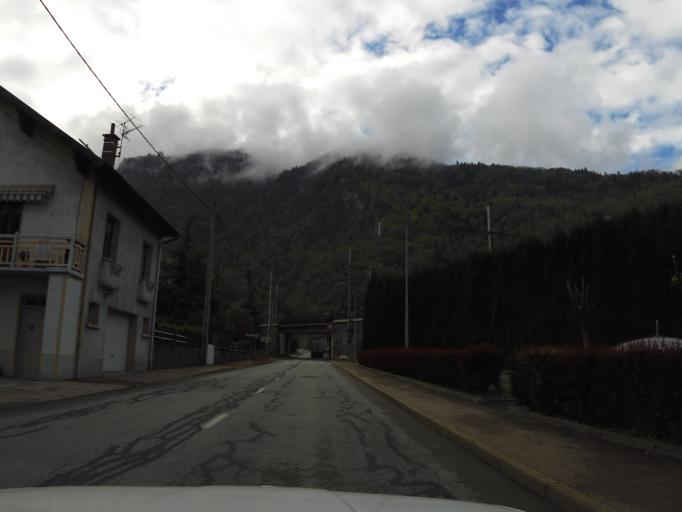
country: FR
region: Rhone-Alpes
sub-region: Departement de la Savoie
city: Saint-Michel-de-Maurienne
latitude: 45.2123
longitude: 6.4780
